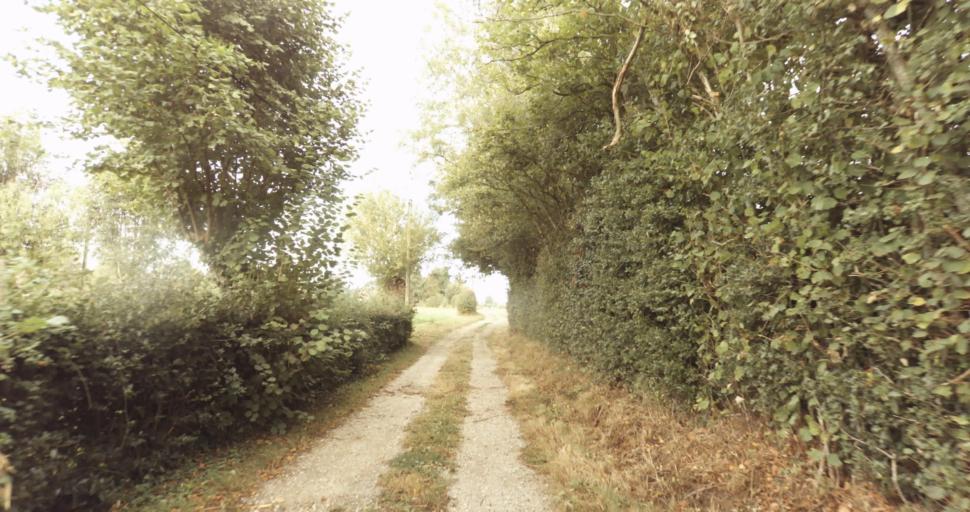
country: FR
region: Lower Normandy
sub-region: Departement de l'Orne
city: Vimoutiers
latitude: 48.9095
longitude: 0.2407
